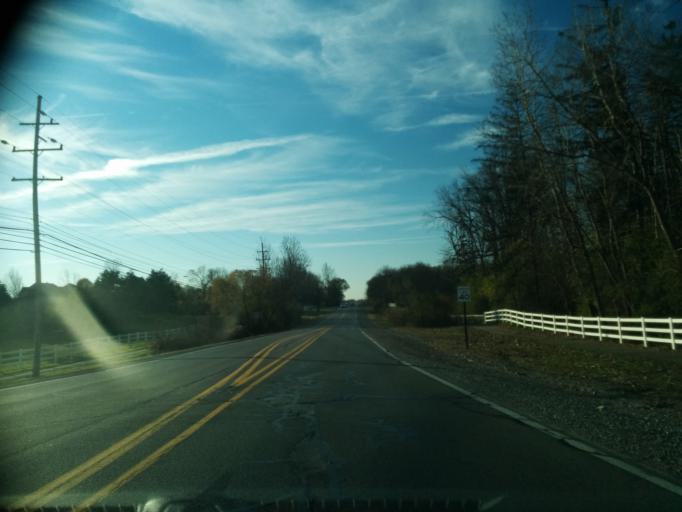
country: US
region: Michigan
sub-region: Oakland County
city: Farmington Hills
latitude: 42.4829
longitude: -83.4165
